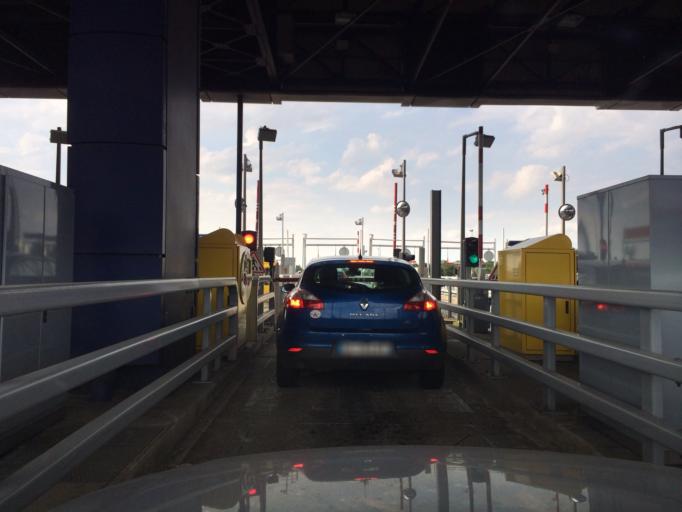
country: FR
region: Haute-Normandie
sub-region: Departement de l'Eure
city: Ande
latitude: 49.1914
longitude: 1.2325
